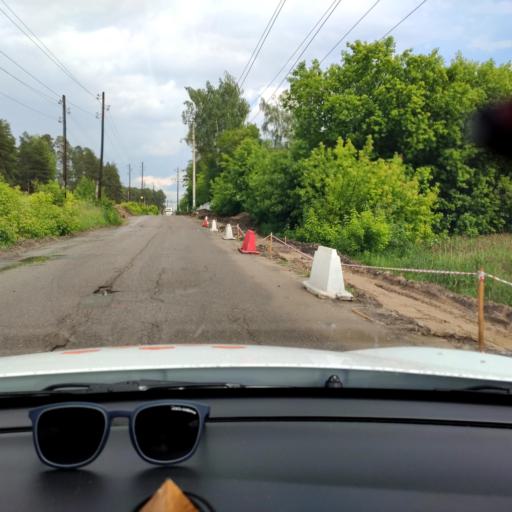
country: RU
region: Tatarstan
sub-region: Zelenodol'skiy Rayon
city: Vasil'yevo
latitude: 55.8369
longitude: 48.6892
